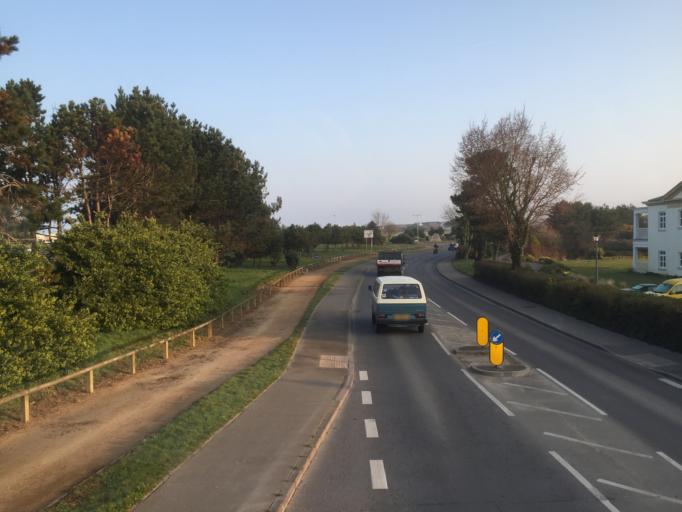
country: JE
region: St Helier
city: Saint Helier
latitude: 49.2048
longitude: -2.1899
